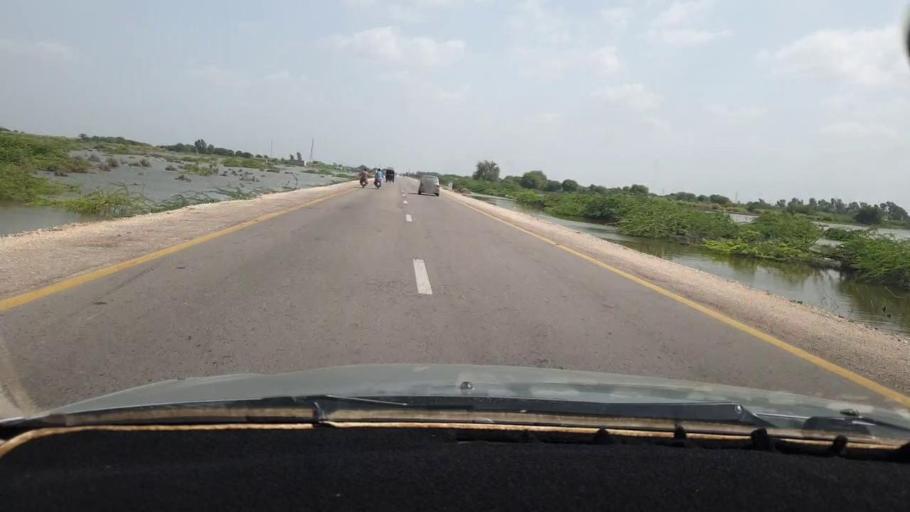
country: PK
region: Sindh
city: Digri
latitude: 25.1234
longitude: 69.1474
